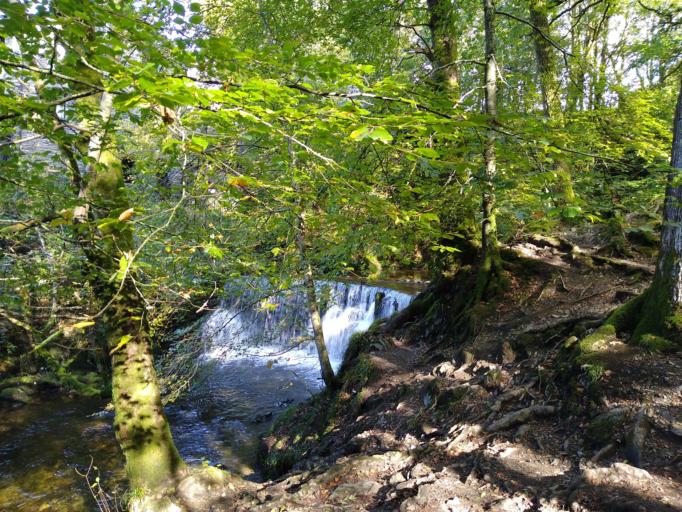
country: GB
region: England
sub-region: Cumbria
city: Ambleside
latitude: 54.4326
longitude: -2.9561
